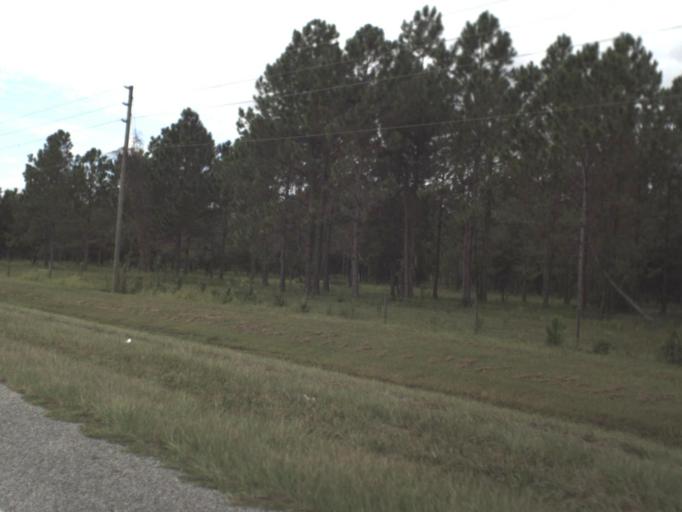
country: US
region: Florida
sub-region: Hardee County
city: Bowling Green
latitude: 27.6949
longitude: -81.8120
